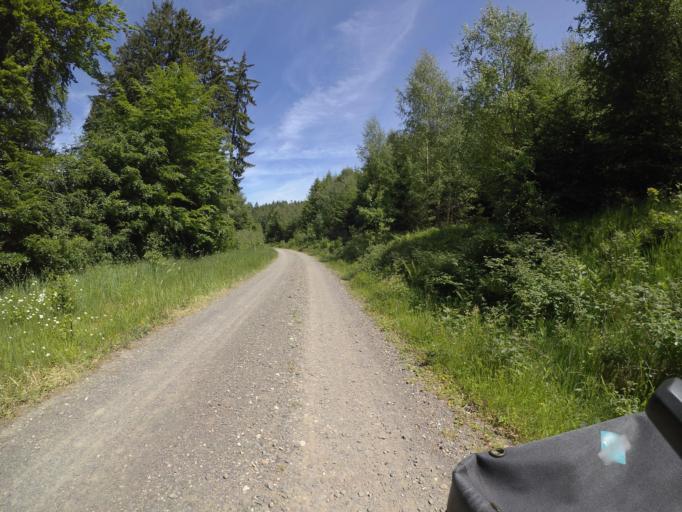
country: DE
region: Rheinland-Pfalz
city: Wirschweiler
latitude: 49.7592
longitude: 7.1137
